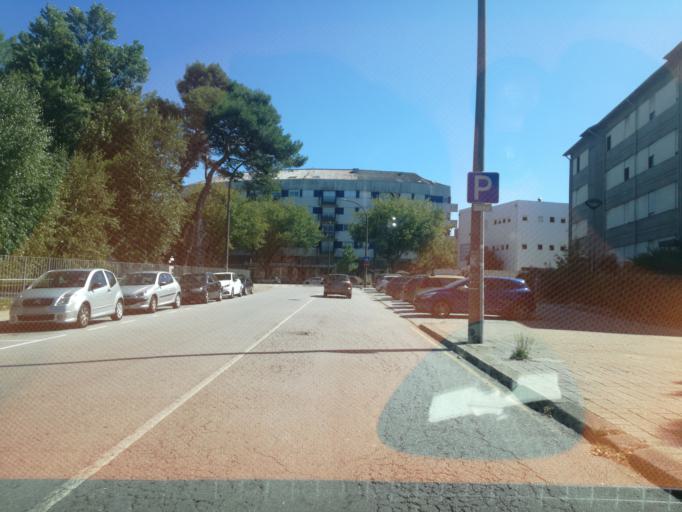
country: PT
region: Porto
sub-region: Matosinhos
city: Sao Mamede de Infesta
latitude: 41.1781
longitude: -8.6093
